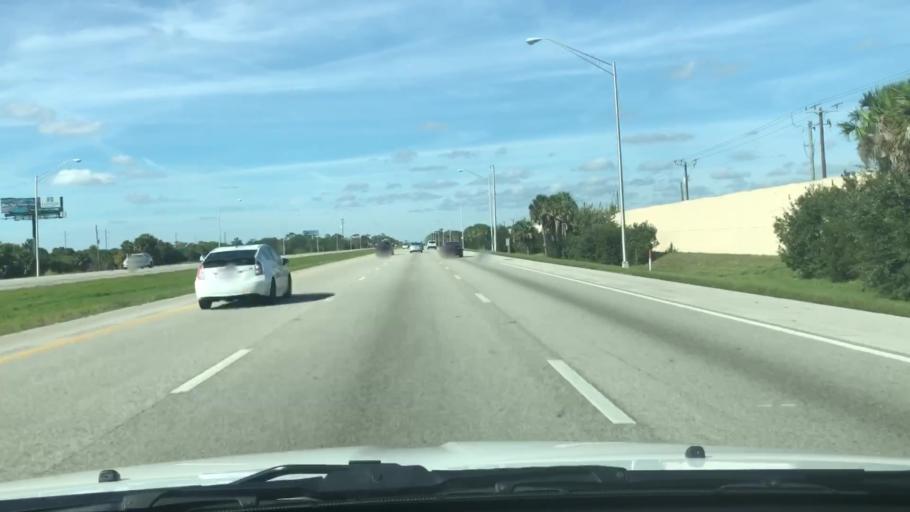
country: US
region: Florida
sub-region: Saint Lucie County
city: Lakewood Park
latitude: 27.5509
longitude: -80.4740
